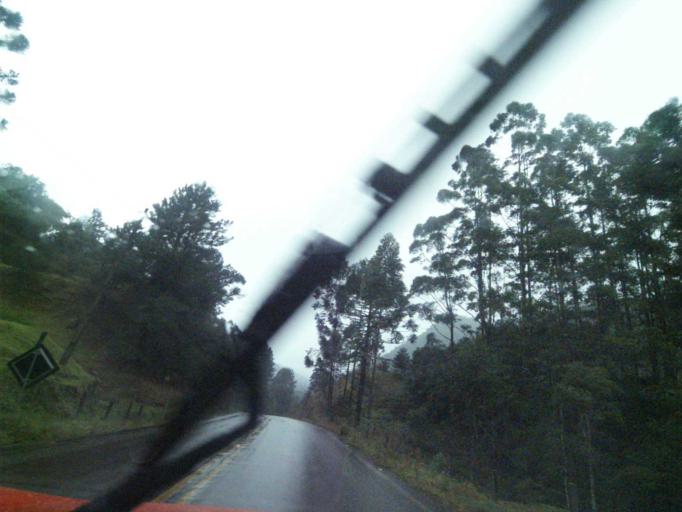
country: BR
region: Santa Catarina
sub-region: Anitapolis
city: Anitapolis
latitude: -27.8023
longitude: -49.0461
